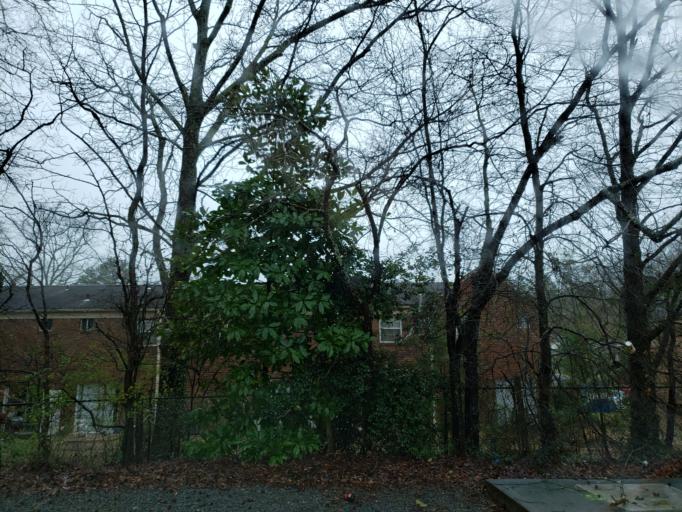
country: US
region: Georgia
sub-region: Cobb County
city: Fair Oaks
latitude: 33.9041
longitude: -84.5371
